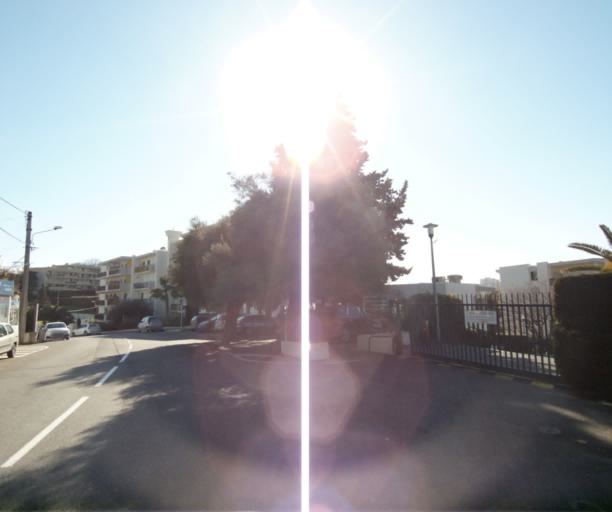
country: FR
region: Provence-Alpes-Cote d'Azur
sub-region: Departement des Alpes-Maritimes
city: Antibes
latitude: 43.5923
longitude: 7.1095
